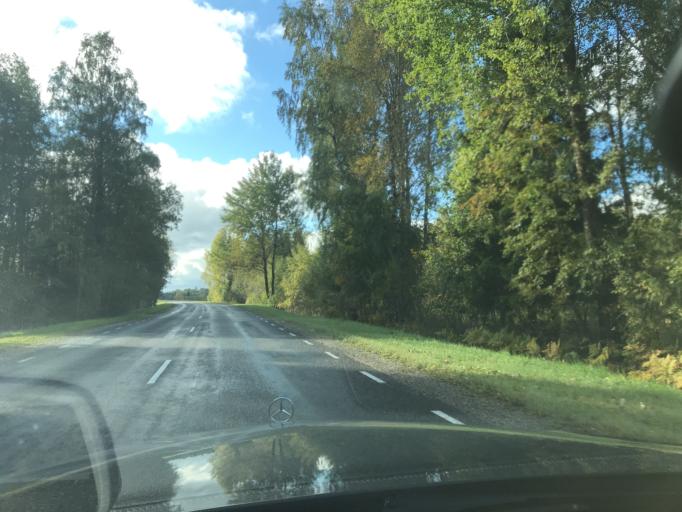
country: EE
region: Tartu
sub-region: Elva linn
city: Elva
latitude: 57.9926
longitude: 26.2643
